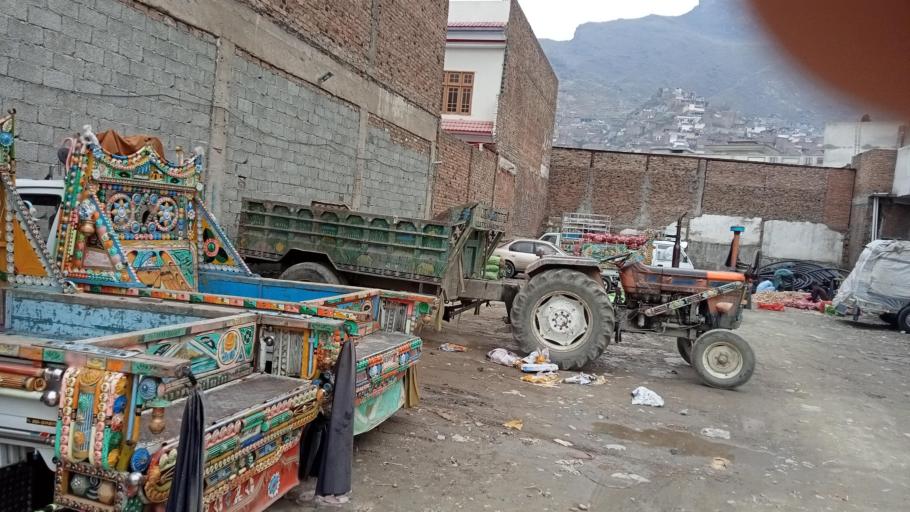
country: PK
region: Khyber Pakhtunkhwa
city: Mingora
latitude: 34.7688
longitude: 72.3383
